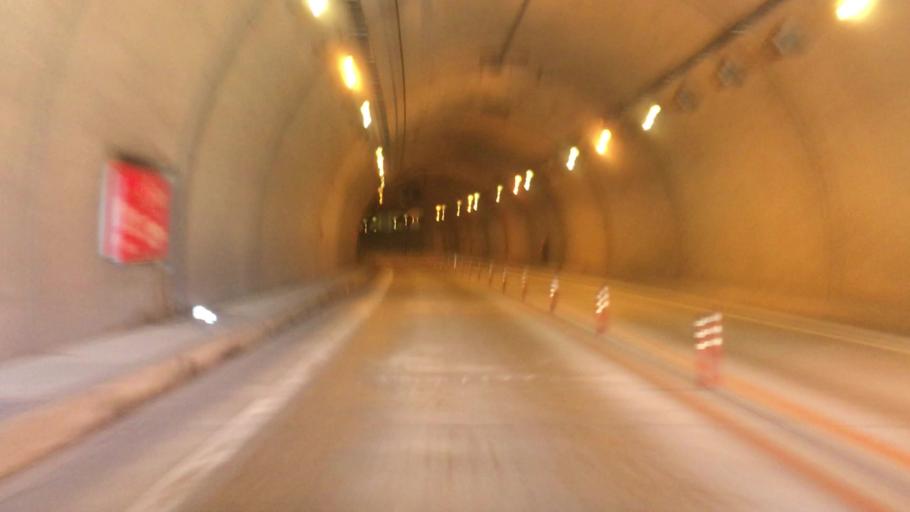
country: JP
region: Tottori
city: Tottori
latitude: 35.3019
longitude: 134.2012
